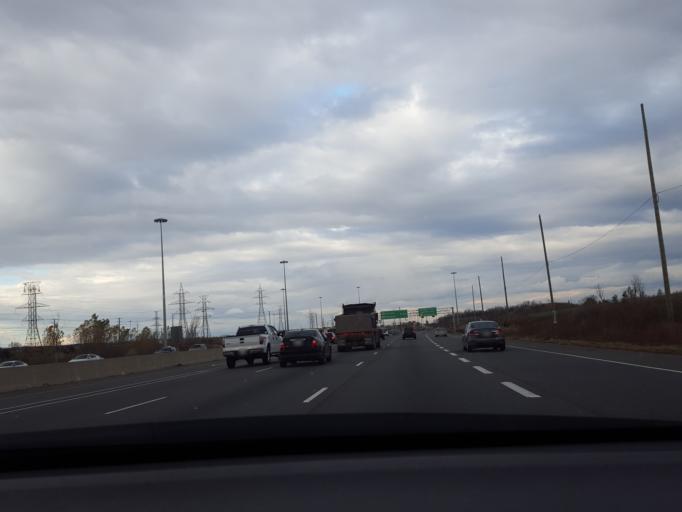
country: CA
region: Ontario
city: Mississauga
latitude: 43.6084
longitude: -79.6360
